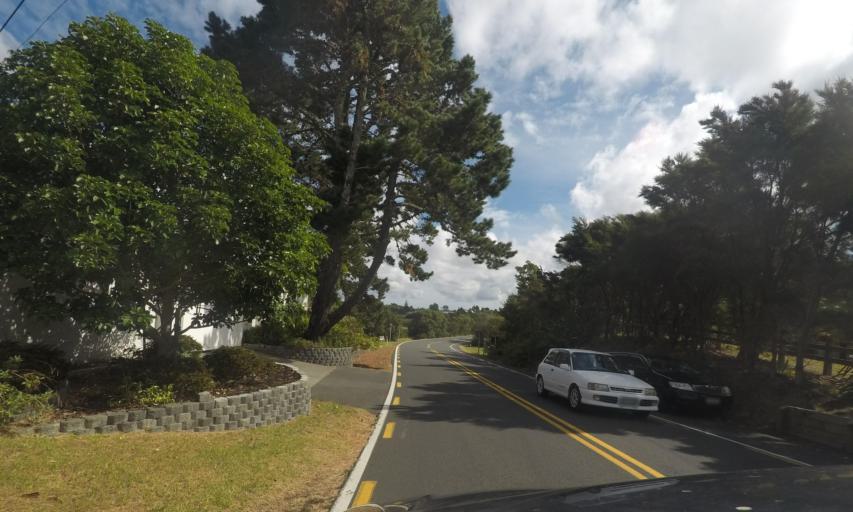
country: NZ
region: Auckland
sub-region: Auckland
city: Rosebank
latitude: -36.7813
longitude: 174.6509
